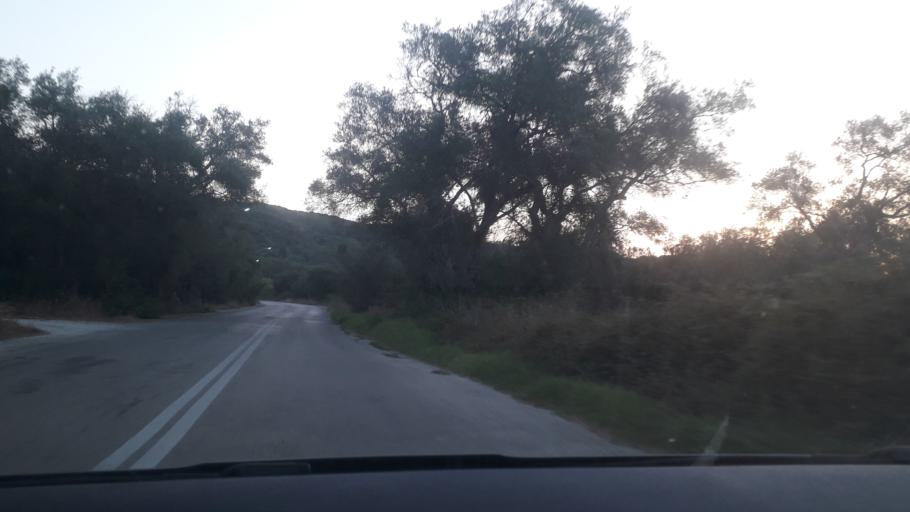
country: GR
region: Ionian Islands
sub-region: Nomos Kerkyras
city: Perivoli
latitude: 39.4394
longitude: 19.9524
